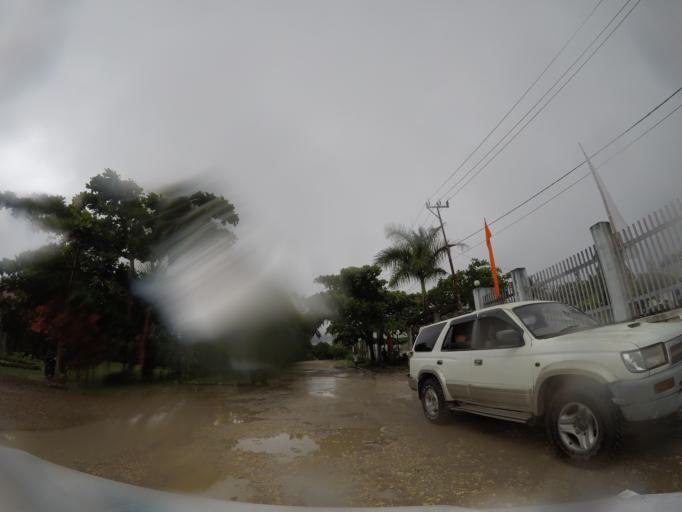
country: TL
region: Baucau
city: Venilale
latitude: -8.6425
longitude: 126.3792
